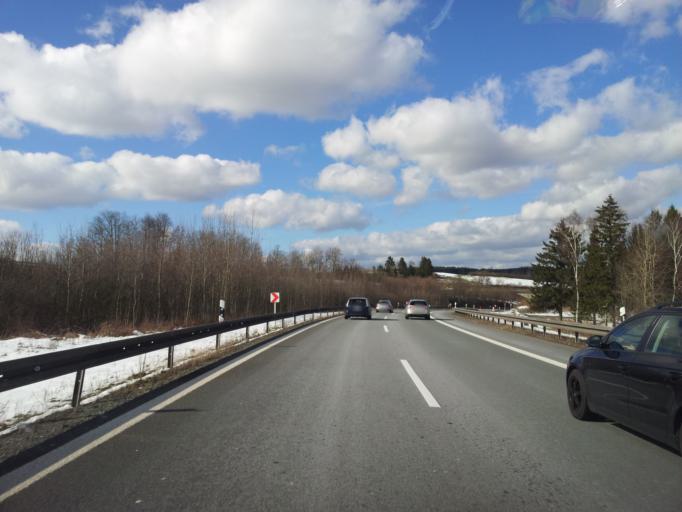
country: DE
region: Bavaria
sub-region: Upper Franconia
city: Leupoldsgrun
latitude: 50.3220
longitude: 11.7942
